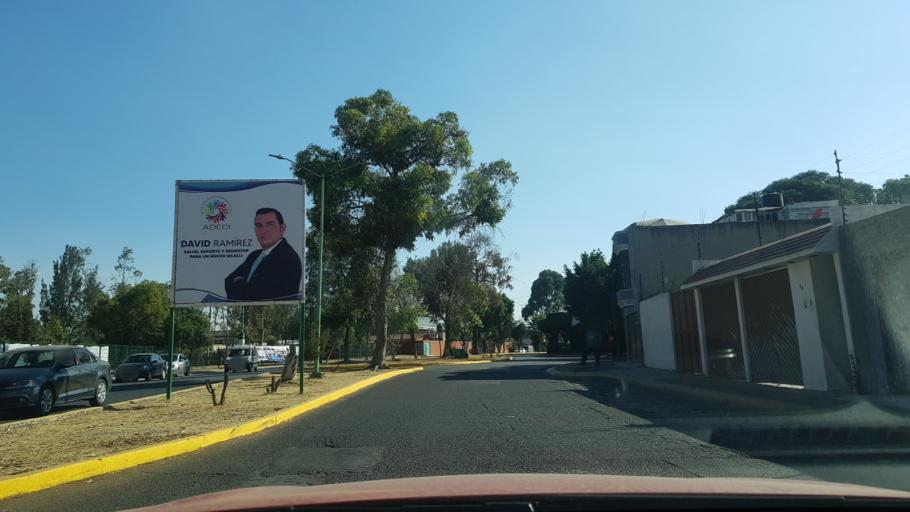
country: MX
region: Mexico
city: Cuautitlan Izcalli
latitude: 19.6409
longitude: -99.1998
